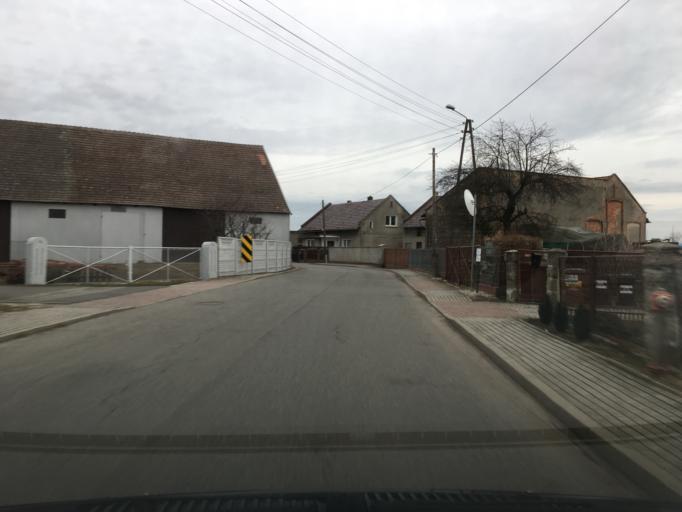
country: PL
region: Opole Voivodeship
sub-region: Powiat kedzierzynsko-kozielski
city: Kozle
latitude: 50.3550
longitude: 18.1262
